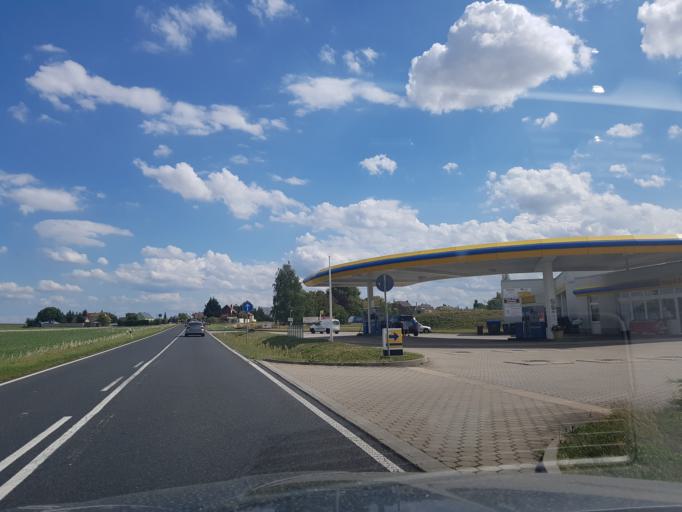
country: DE
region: Saxony
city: Grossenhain
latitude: 51.2692
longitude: 13.5348
